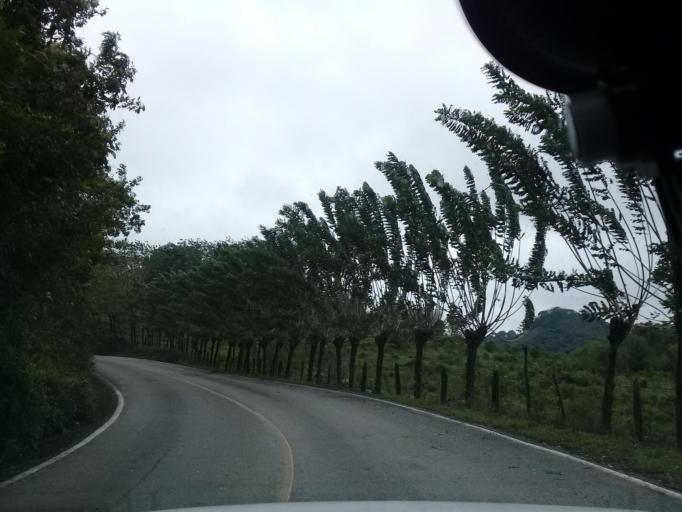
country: MX
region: Veracruz
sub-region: Chalma
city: San Pedro Coyutla
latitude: 21.2138
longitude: -98.4260
